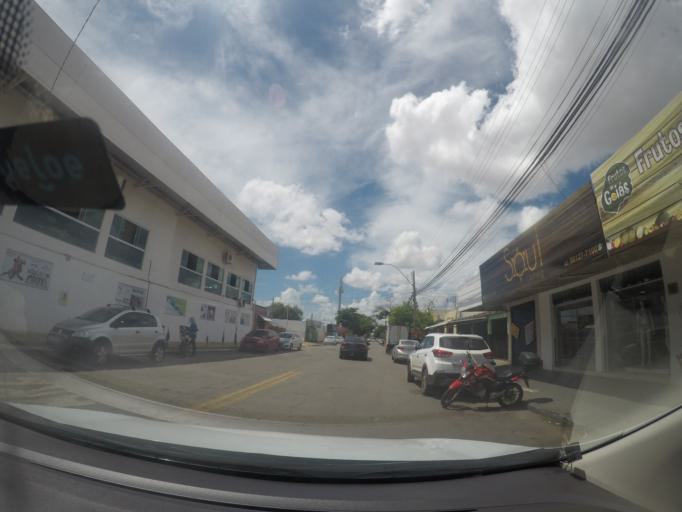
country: BR
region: Goias
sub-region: Goiania
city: Goiania
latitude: -16.6806
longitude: -49.3162
